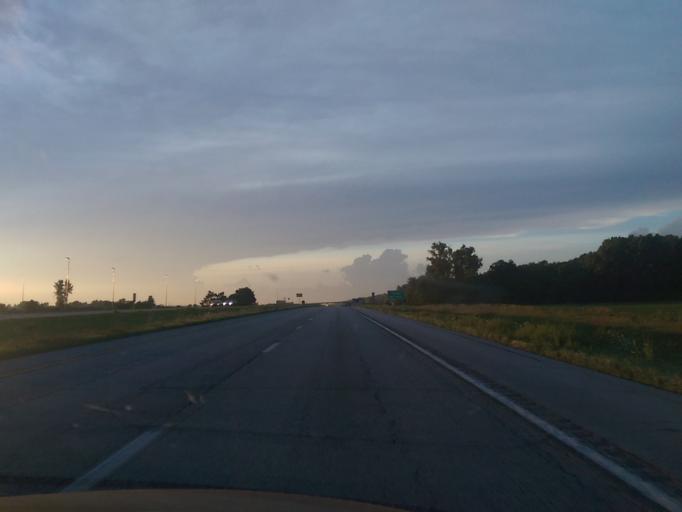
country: US
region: Missouri
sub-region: Atchison County
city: Rock Port
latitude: 40.3935
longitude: -95.5477
